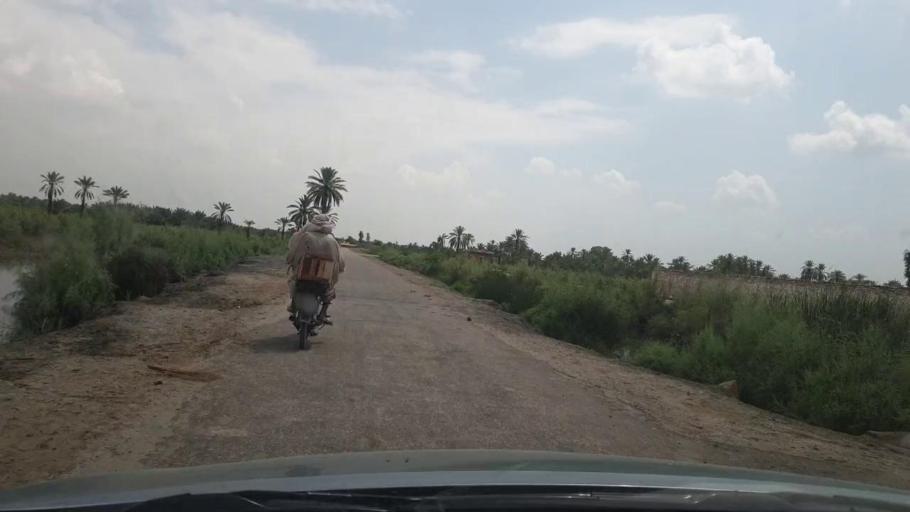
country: PK
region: Sindh
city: Kot Diji
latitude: 27.4043
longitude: 68.7388
